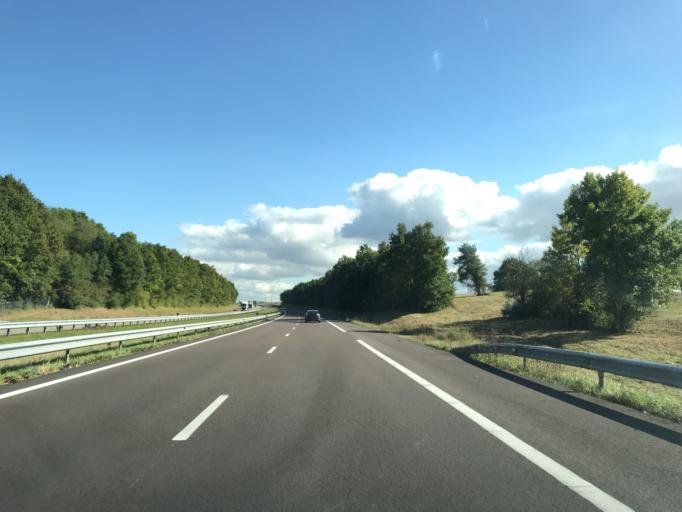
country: FR
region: Ile-de-France
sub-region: Departement de Seine-et-Marne
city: Egreville
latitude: 48.1403
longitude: 2.9134
